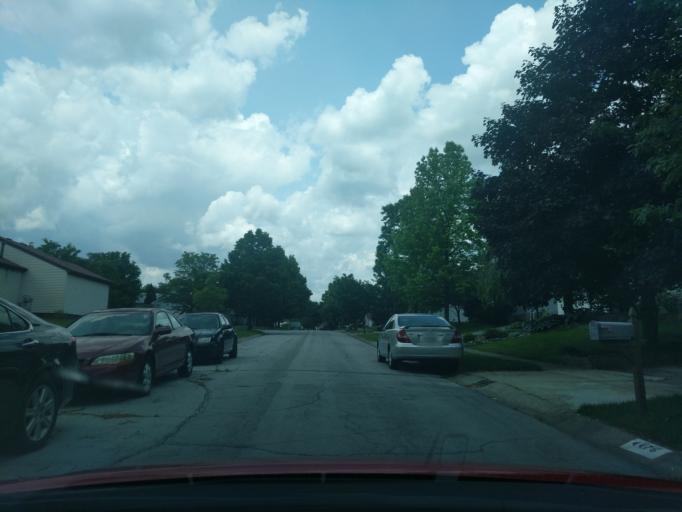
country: US
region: Ohio
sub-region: Franklin County
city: Huber Ridge
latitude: 40.0637
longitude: -82.9165
